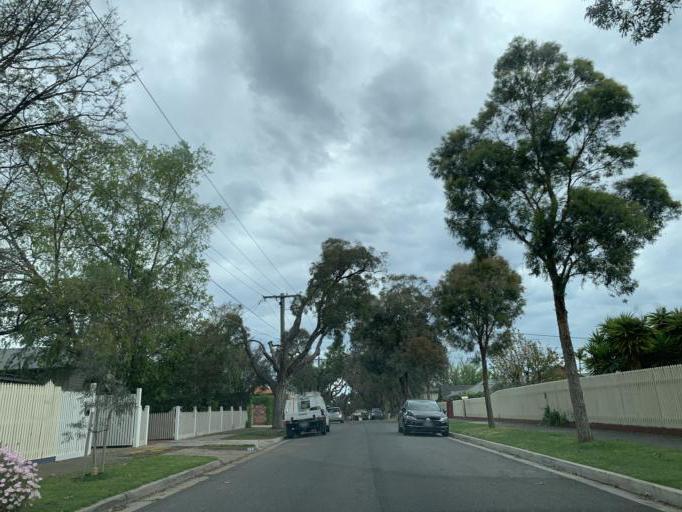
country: AU
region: Victoria
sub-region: Bayside
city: Hampton East
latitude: -37.9328
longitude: 145.0193
